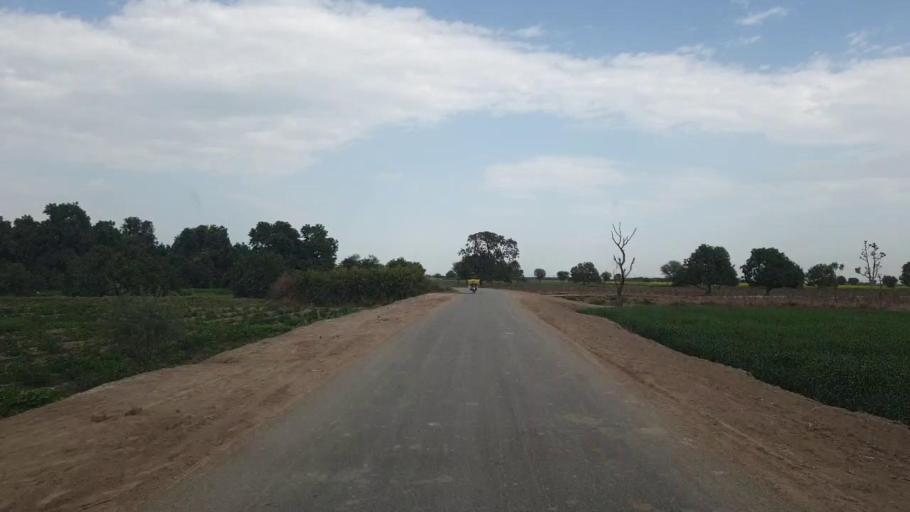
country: PK
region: Sindh
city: Hala
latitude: 25.9658
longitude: 68.3966
